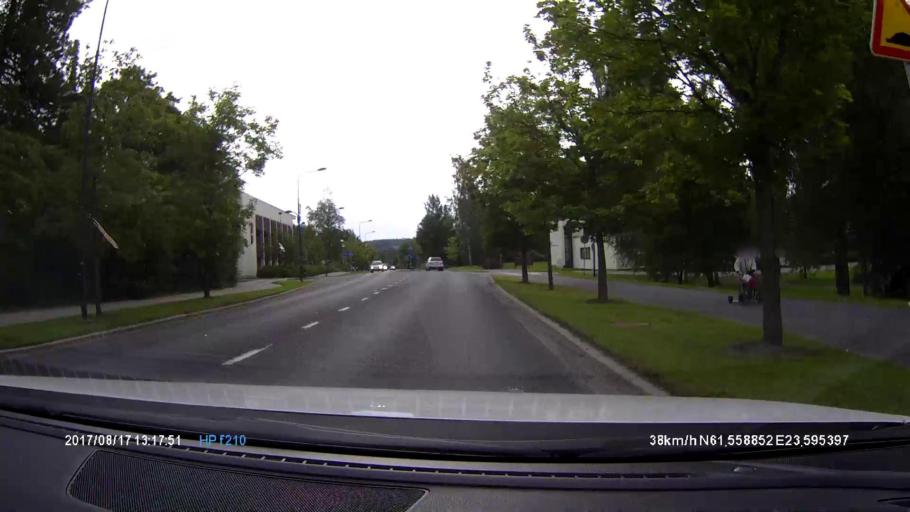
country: FI
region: Pirkanmaa
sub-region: Tampere
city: Yloejaervi
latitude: 61.5589
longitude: 23.5953
